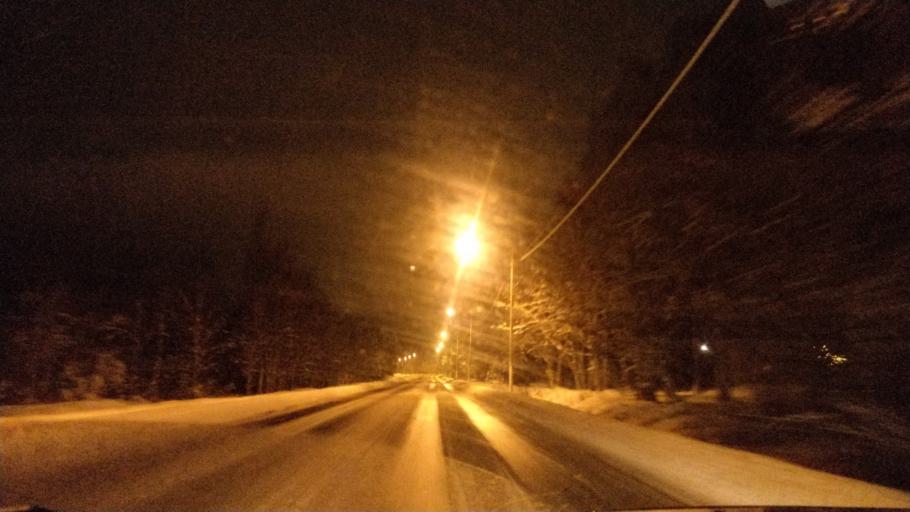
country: FI
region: Lapland
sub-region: Rovaniemi
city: Rovaniemi
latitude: 66.3827
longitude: 25.3781
